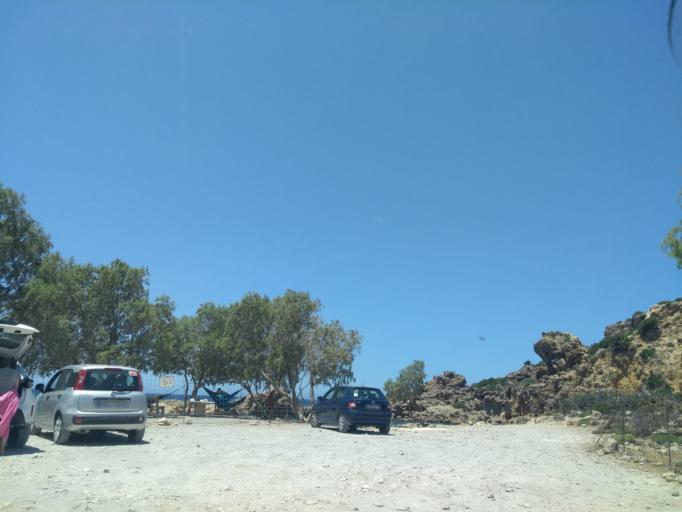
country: GR
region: Crete
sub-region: Nomos Chanias
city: Vryses
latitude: 35.3149
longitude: 23.5342
